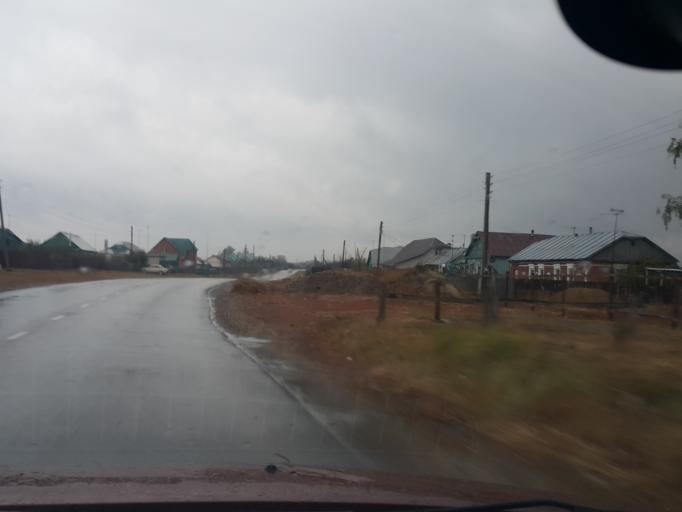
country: RU
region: Tambov
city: Kotovsk
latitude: 52.5325
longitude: 41.4759
